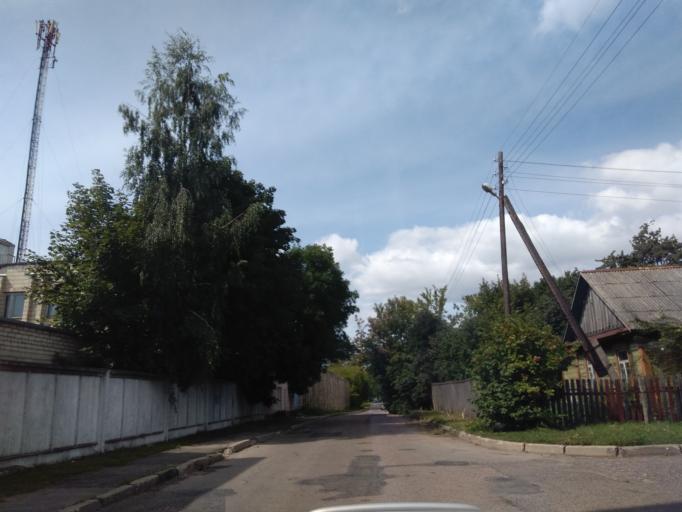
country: BY
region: Minsk
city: Syenitsa
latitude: 53.8781
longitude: 27.5109
